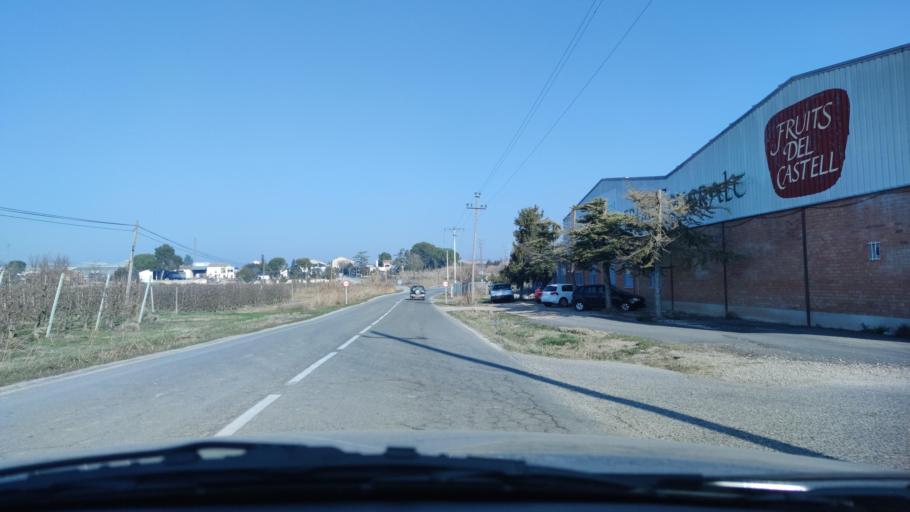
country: ES
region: Catalonia
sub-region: Provincia de Lleida
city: Aspa
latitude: 41.5490
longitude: 0.7347
